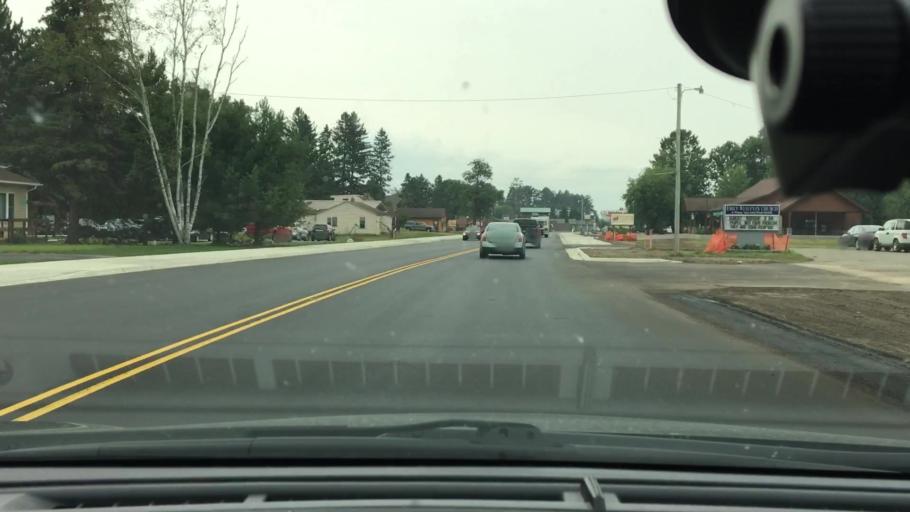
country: US
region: Minnesota
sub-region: Crow Wing County
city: Cross Lake
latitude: 46.7335
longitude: -93.9580
